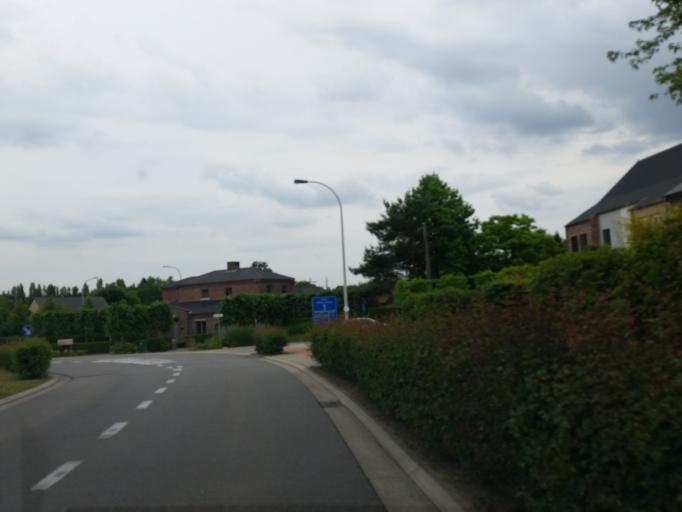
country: BE
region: Flanders
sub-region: Provincie Antwerpen
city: Lier
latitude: 51.1597
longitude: 4.5913
